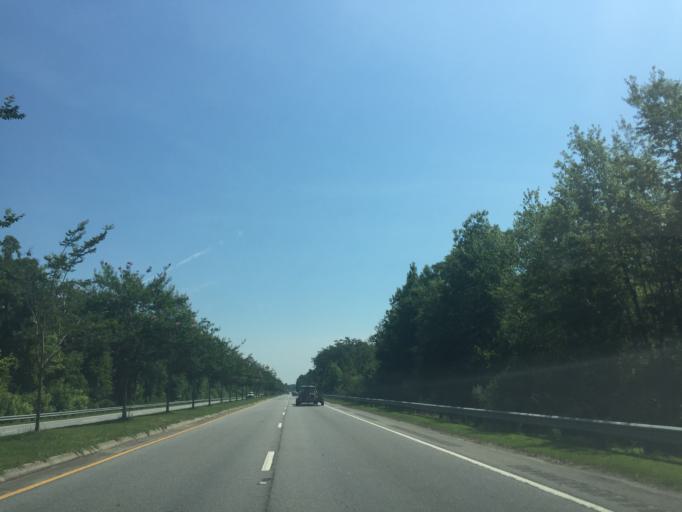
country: US
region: Georgia
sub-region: Bryan County
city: Richmond Hill
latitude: 31.9680
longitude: -81.2979
